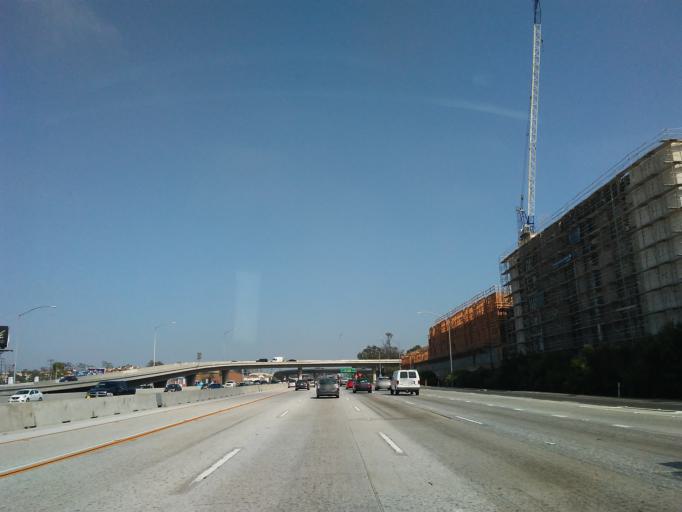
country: US
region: California
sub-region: Los Angeles County
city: Ladera Heights
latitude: 33.9767
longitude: -118.3878
